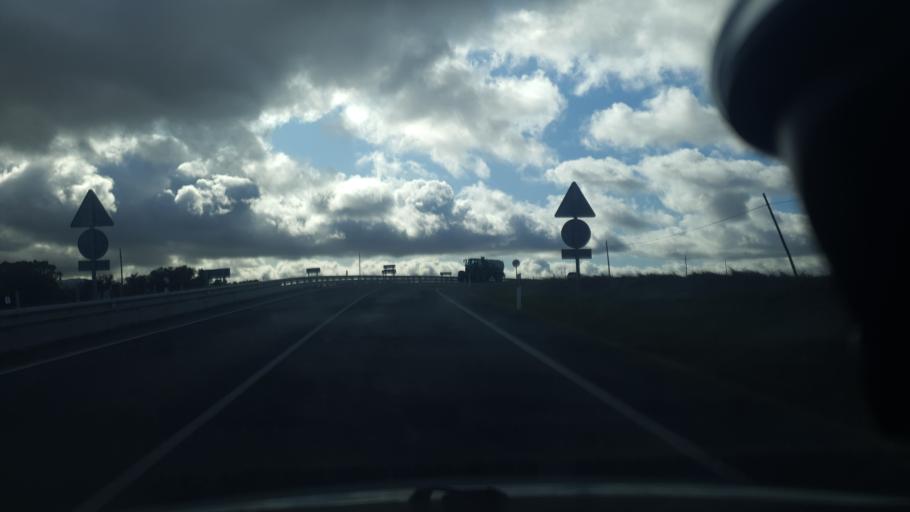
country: ES
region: Castille and Leon
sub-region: Provincia de Segovia
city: Ortigosa del Monte
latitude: 40.8863
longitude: -4.2046
